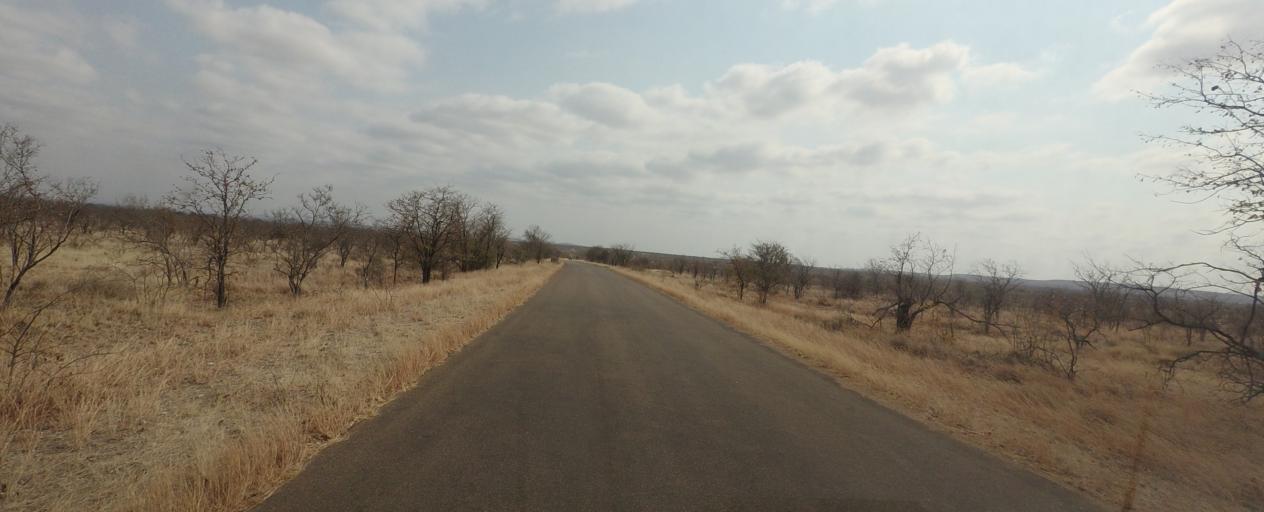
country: ZA
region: Limpopo
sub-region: Vhembe District Municipality
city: Mutale
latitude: -22.5669
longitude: 31.1919
